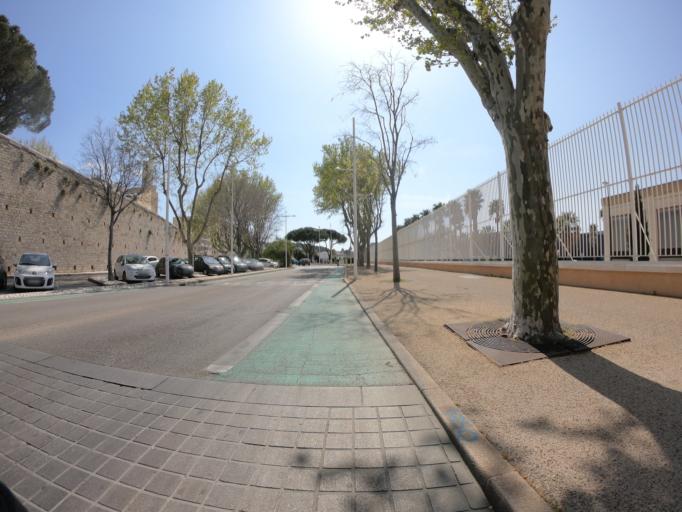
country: FR
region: Provence-Alpes-Cote d'Azur
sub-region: Departement du Var
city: Toulon
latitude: 43.1091
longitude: 5.9311
